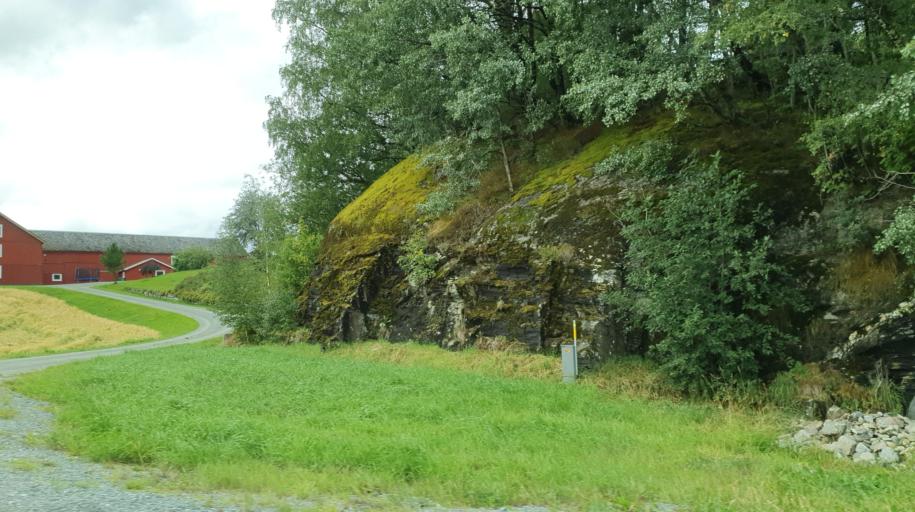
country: NO
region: Nord-Trondelag
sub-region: Stjordal
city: Stjordalshalsen
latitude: 63.4287
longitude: 10.9554
